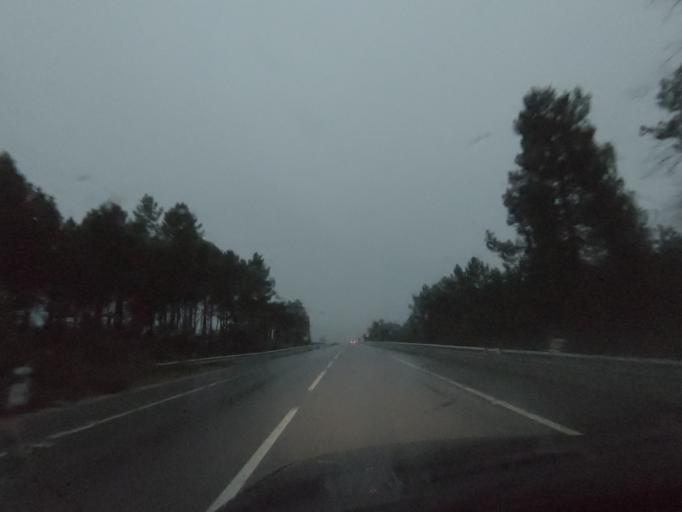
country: PT
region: Vila Real
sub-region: Sabrosa
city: Vilela
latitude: 41.2638
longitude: -7.6255
